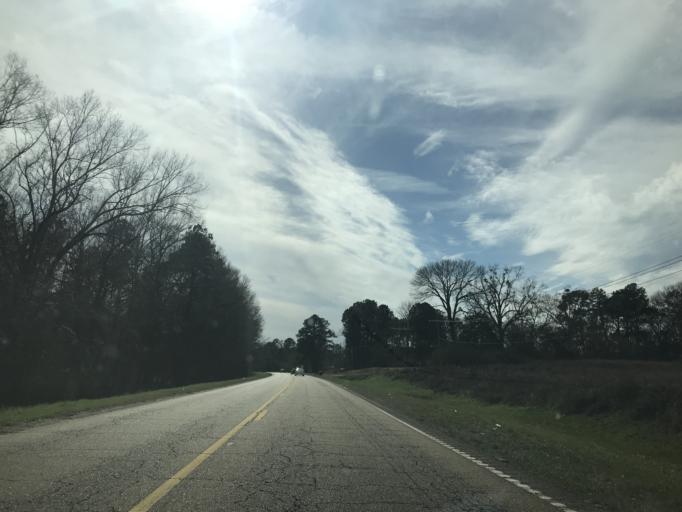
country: US
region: Mississippi
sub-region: Hinds County
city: Edwards
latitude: 32.1045
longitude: -90.6147
